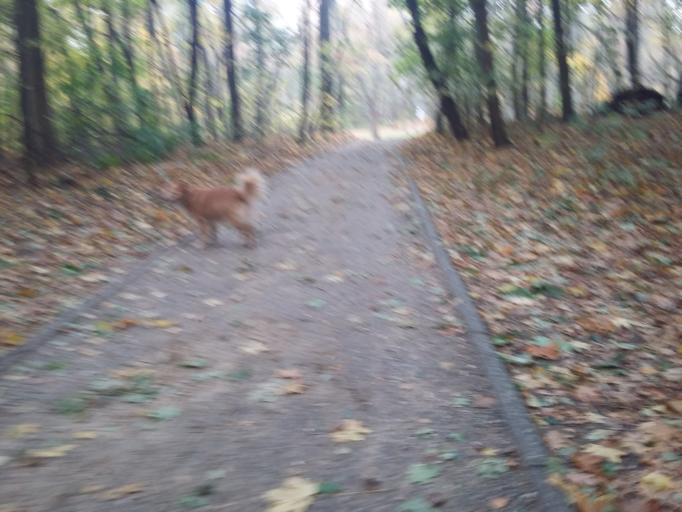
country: PL
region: Lodz Voivodeship
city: Lodz
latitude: 51.7623
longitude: 19.4189
